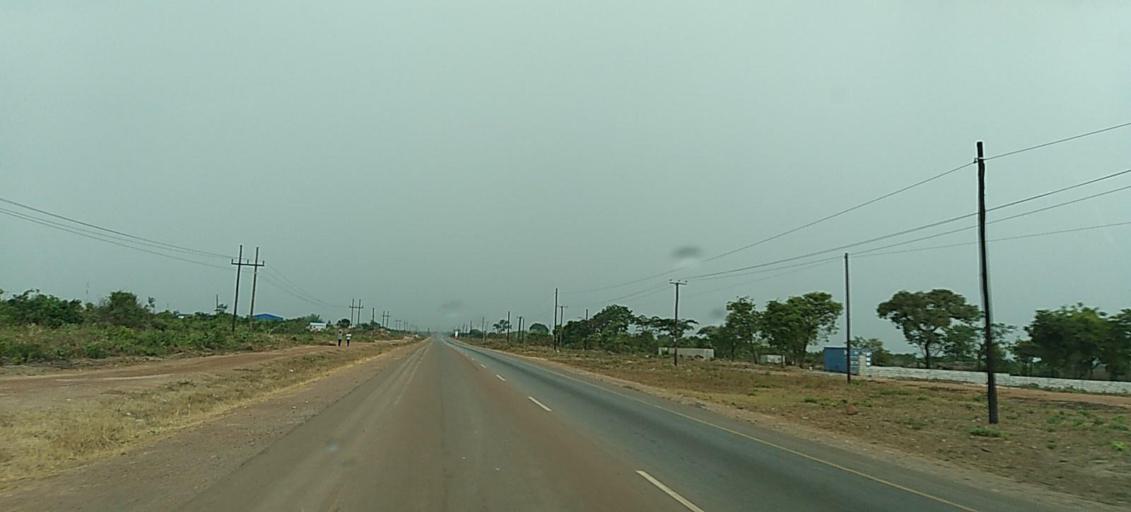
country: ZM
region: Copperbelt
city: Kalulushi
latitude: -12.8348
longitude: 28.1193
